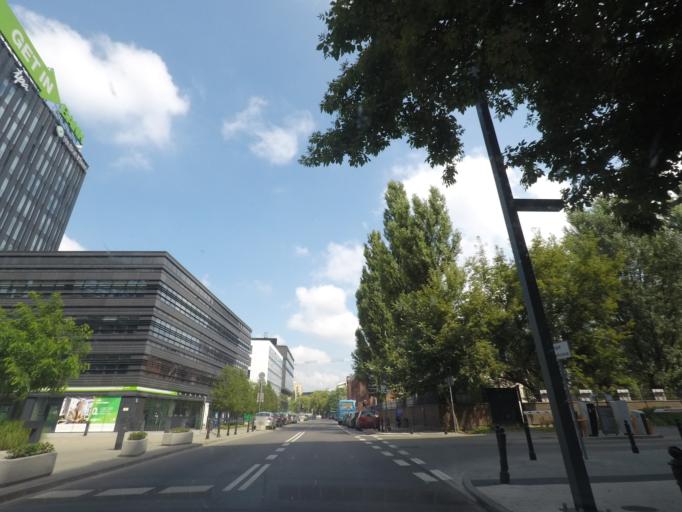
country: PL
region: Masovian Voivodeship
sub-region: Warszawa
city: Ochota
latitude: 52.2313
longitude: 20.9806
